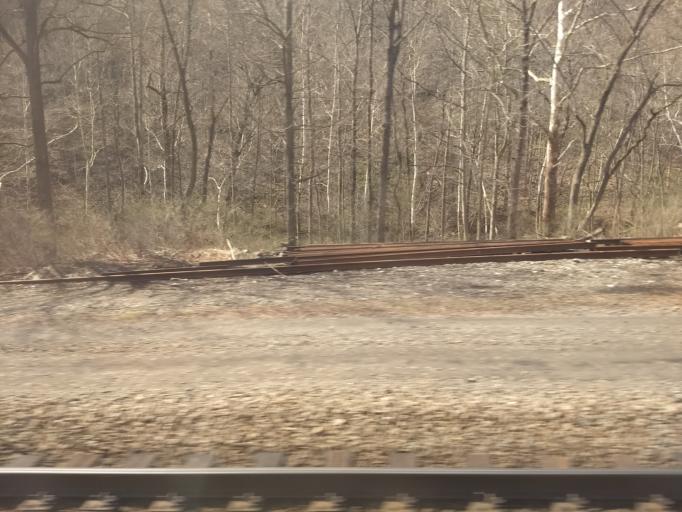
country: US
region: Pennsylvania
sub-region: Blair County
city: Tyrone
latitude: 40.6277
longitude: -78.1788
